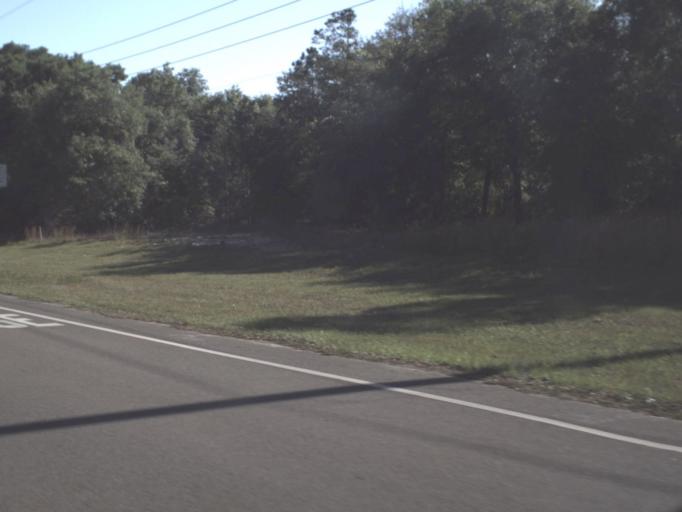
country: US
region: Florida
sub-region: Marion County
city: Dunnellon
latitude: 29.0742
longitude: -82.4530
